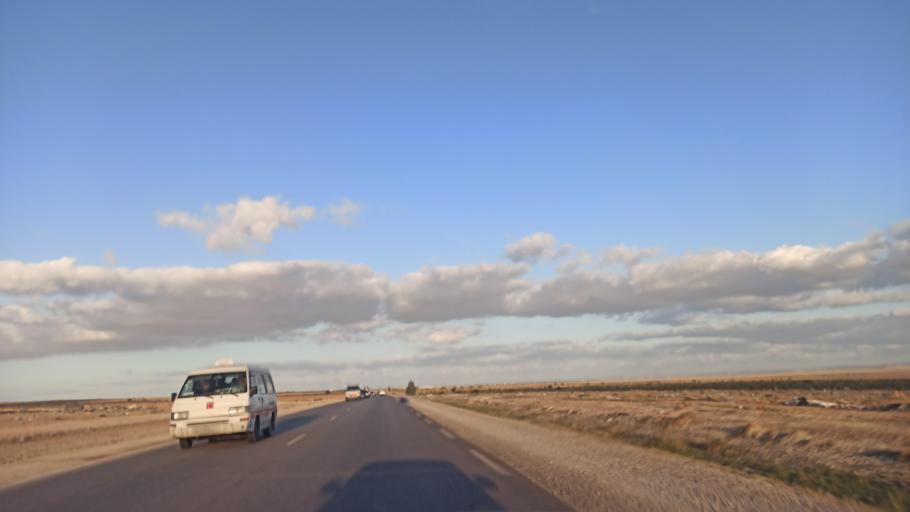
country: TN
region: Al Qayrawan
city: Sbikha
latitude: 35.8883
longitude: 10.2421
